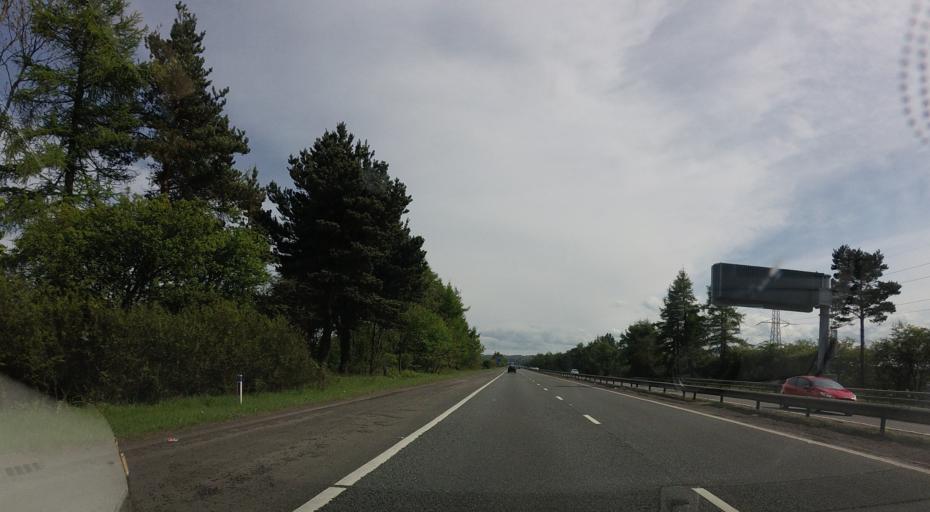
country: GB
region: Scotland
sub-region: Falkirk
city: Falkirk
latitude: 56.0289
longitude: -3.7626
